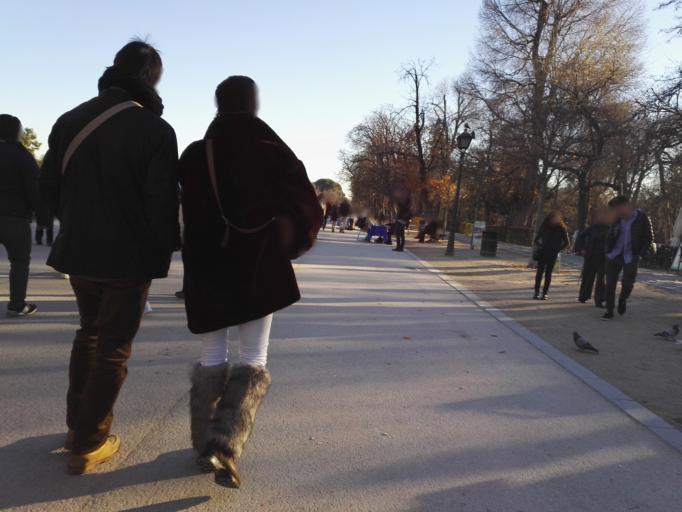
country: ES
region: Madrid
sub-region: Provincia de Madrid
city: Retiro
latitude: 40.4182
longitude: -3.6851
